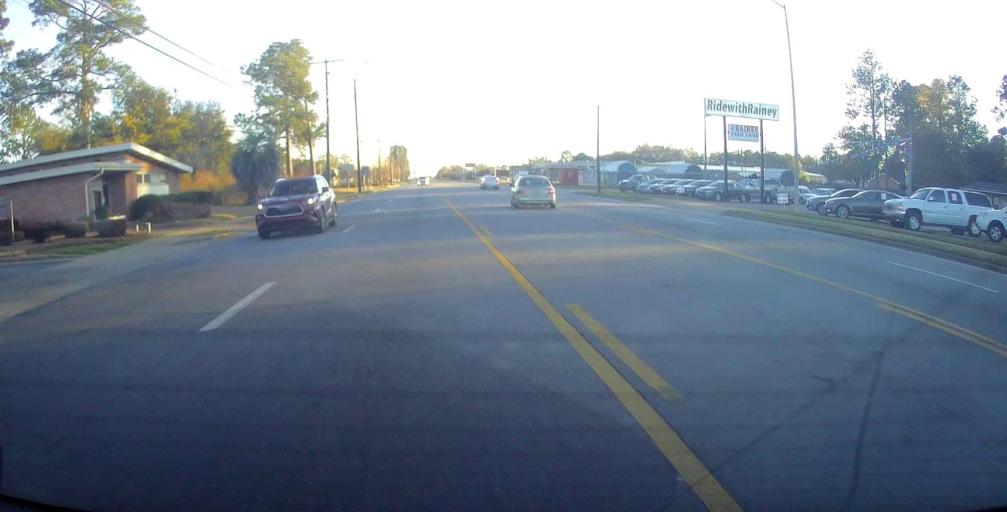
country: US
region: Georgia
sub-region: Dougherty County
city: Albany
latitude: 31.5660
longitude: -84.1763
